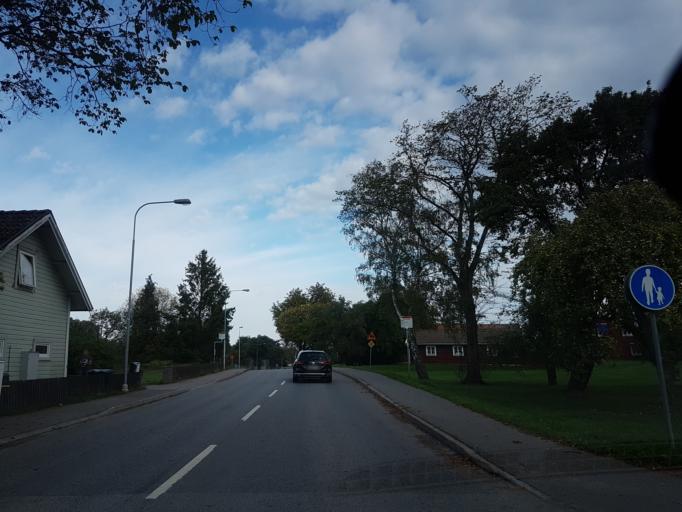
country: SE
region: OEstergoetland
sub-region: Linkopings Kommun
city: Vikingstad
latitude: 58.3794
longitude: 15.4385
